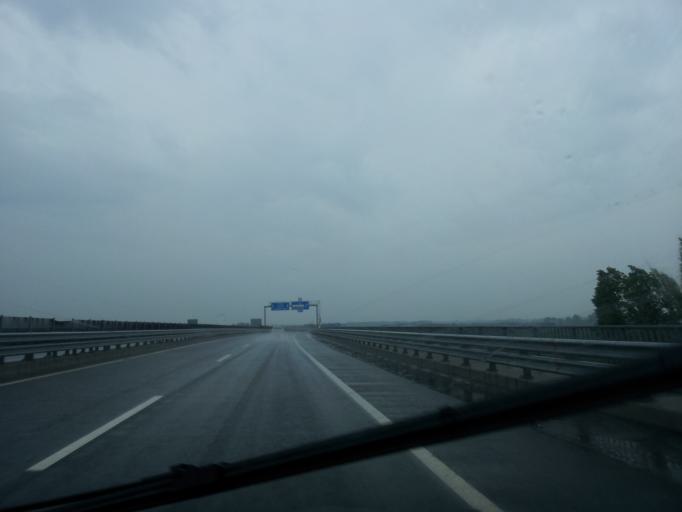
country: HU
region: Tolna
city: Szekszard
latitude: 46.3678
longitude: 18.7510
